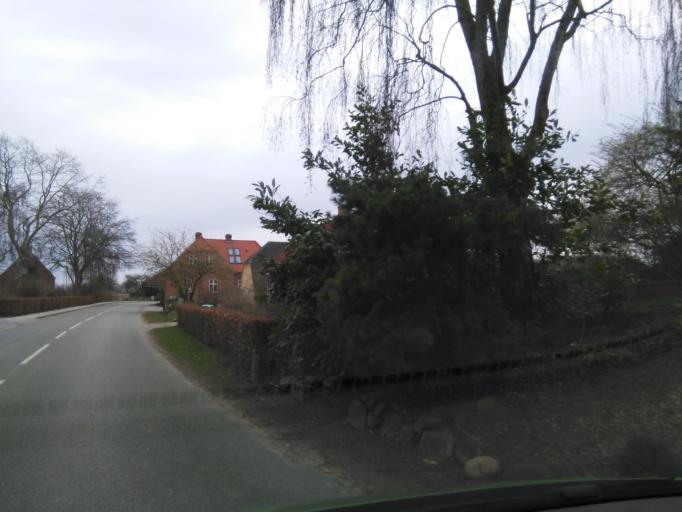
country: DK
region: Central Jutland
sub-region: Arhus Kommune
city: Beder
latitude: 56.0364
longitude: 10.2387
